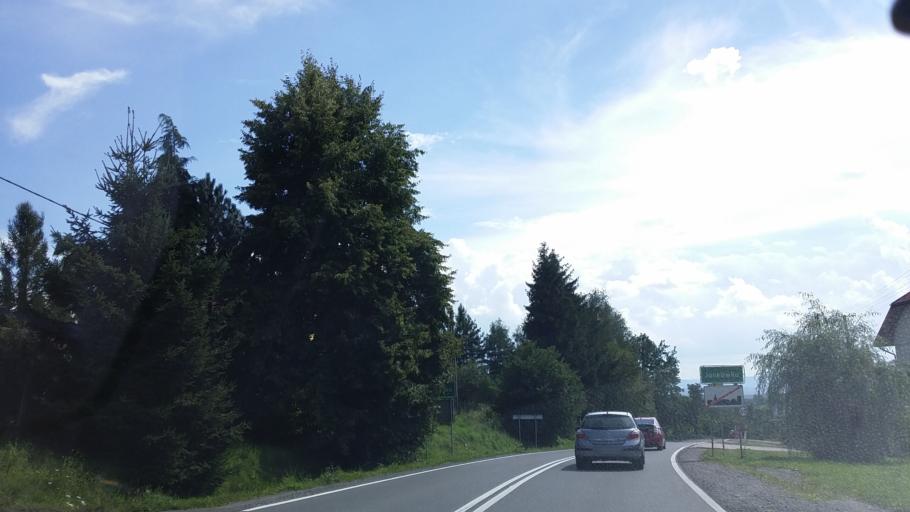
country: PL
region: Lesser Poland Voivodeship
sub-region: Powiat wielicki
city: Pawlikowice
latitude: 49.9351
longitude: 20.0629
